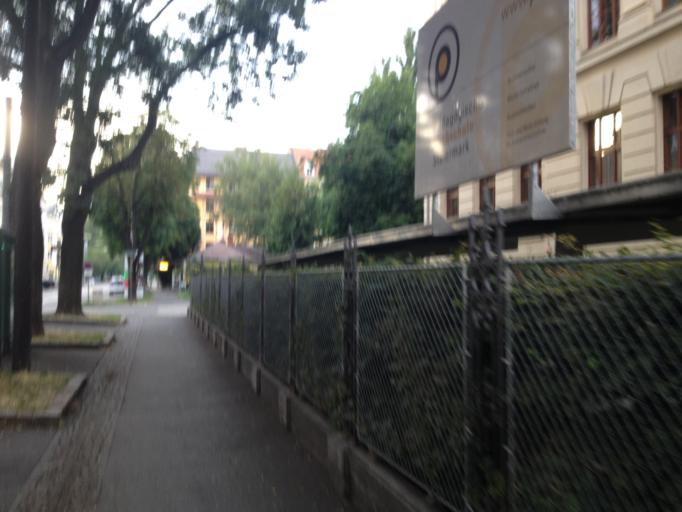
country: AT
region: Styria
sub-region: Graz Stadt
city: Graz
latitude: 47.0821
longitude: 15.4333
